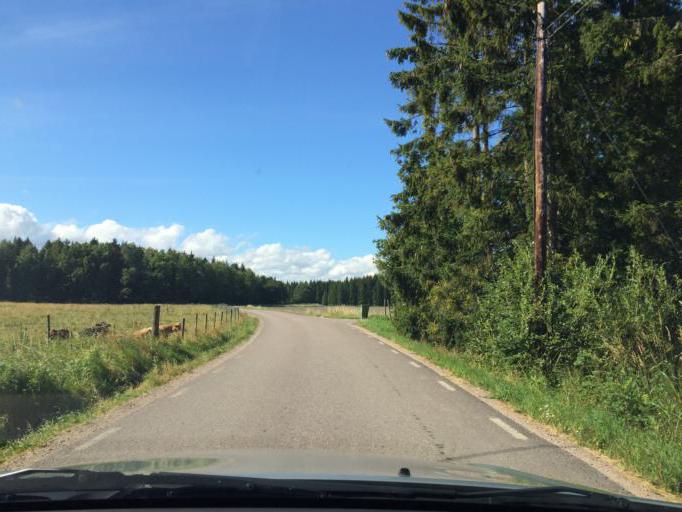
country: SE
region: Soedermanland
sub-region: Eskilstuna Kommun
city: Kvicksund
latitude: 59.5024
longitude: 16.3720
